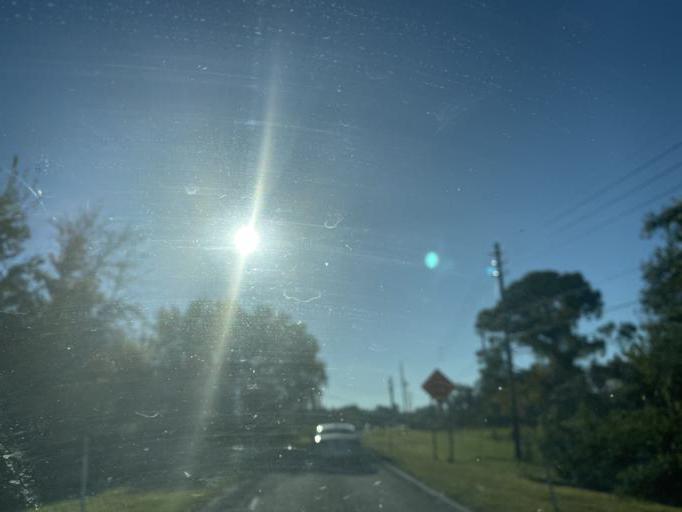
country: US
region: Florida
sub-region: Orange County
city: Tangelo Park
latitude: 28.4518
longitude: -81.4606
